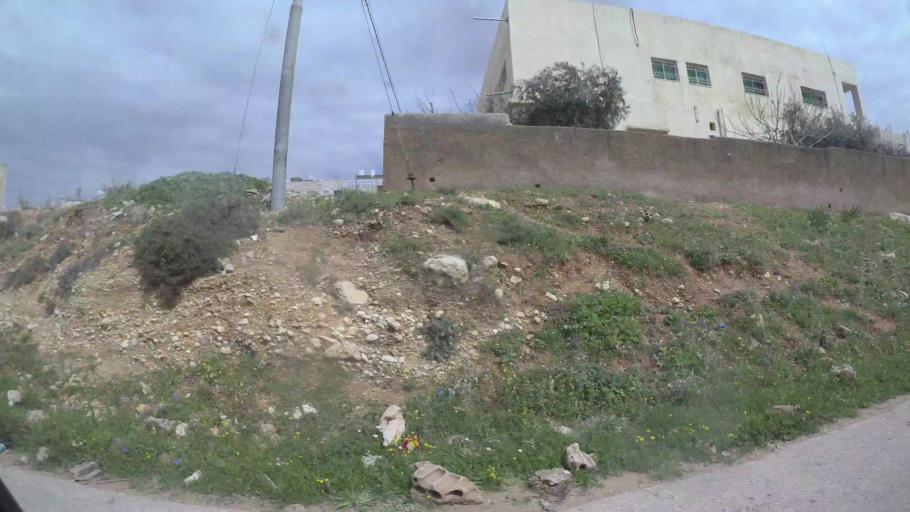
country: JO
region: Amman
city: Al Jubayhah
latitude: 32.0499
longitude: 35.8242
